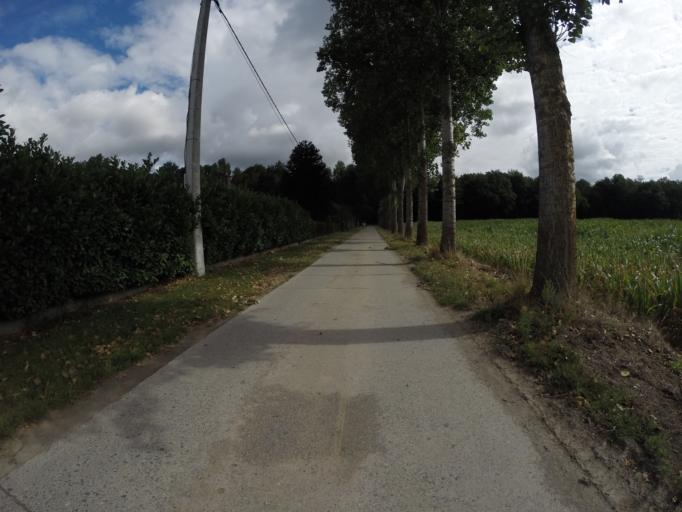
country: BE
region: Flanders
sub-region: Provincie Oost-Vlaanderen
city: Aalter
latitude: 51.1008
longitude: 3.4100
